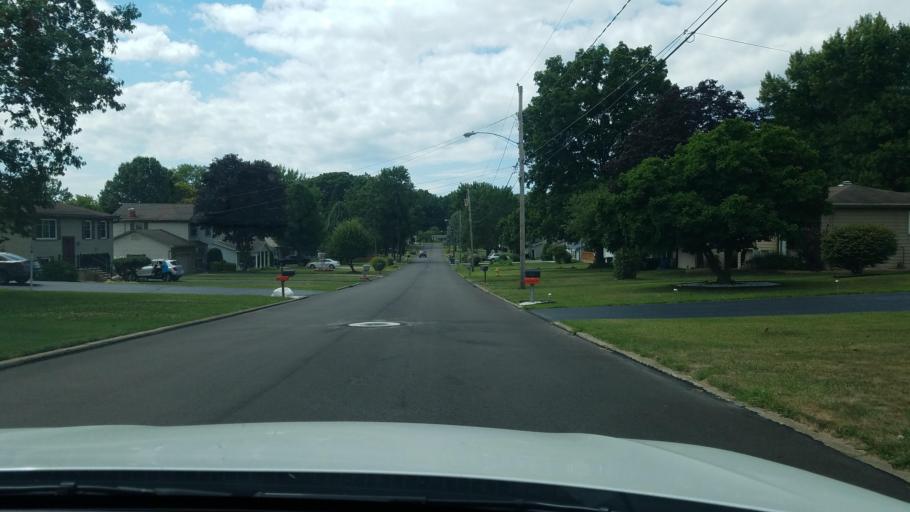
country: US
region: Ohio
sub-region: Trumbull County
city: Mineral Ridge
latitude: 41.1369
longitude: -80.7494
